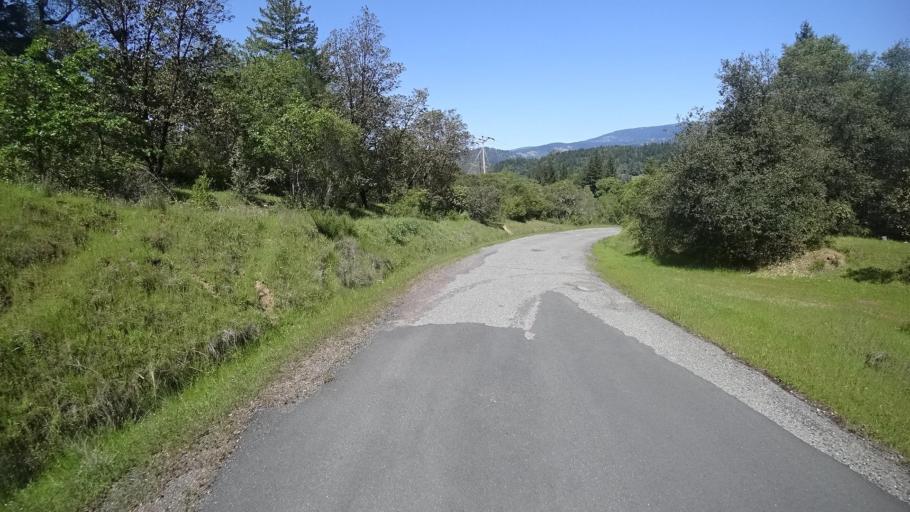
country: US
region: California
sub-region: Humboldt County
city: Redway
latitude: 40.2187
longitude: -123.6485
